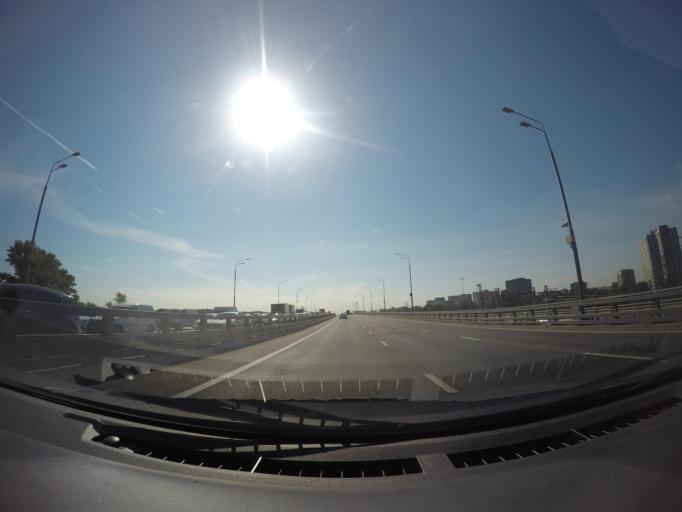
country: RU
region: Moscow
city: Ryazanskiy
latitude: 55.7358
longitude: 37.7676
